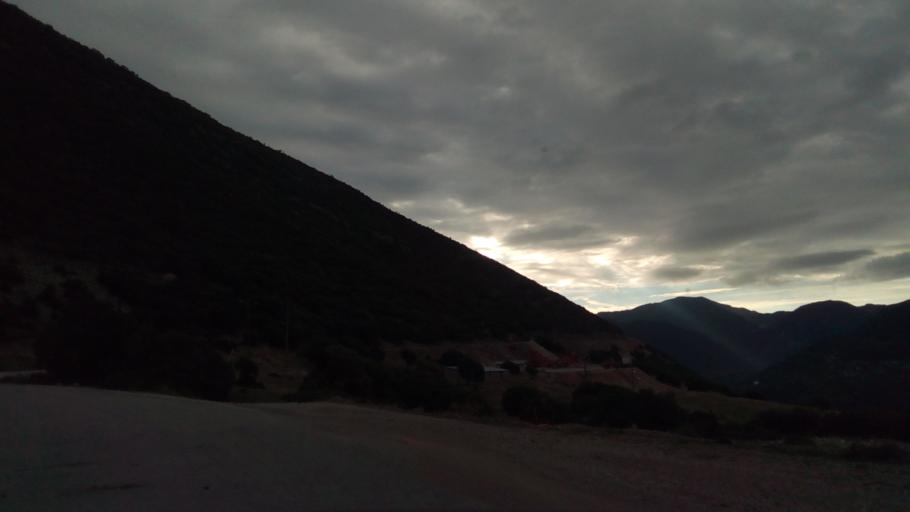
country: GR
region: West Greece
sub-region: Nomos Aitolias kai Akarnanias
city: Thermo
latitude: 38.5974
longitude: 21.8100
